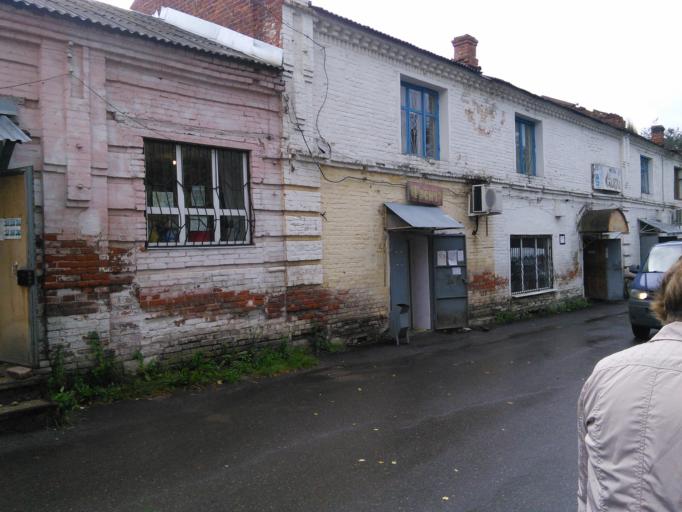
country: RU
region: Jaroslavl
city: Tutayev
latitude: 57.8829
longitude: 39.5433
